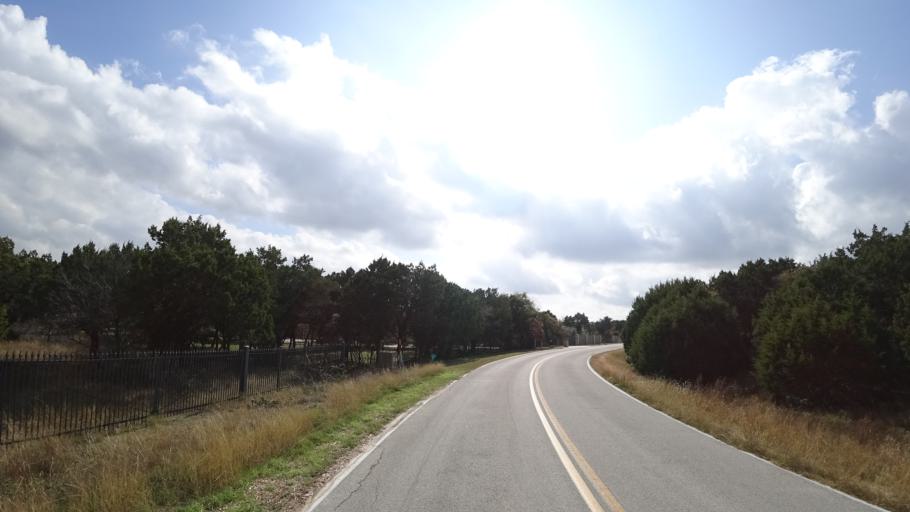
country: US
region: Texas
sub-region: Travis County
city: Barton Creek
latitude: 30.3012
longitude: -97.8709
